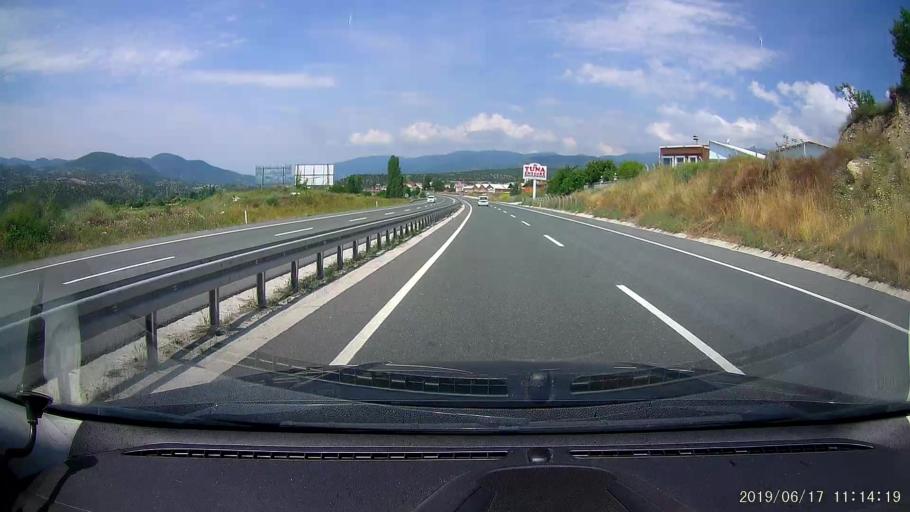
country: TR
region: Kastamonu
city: Tosya
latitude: 40.9576
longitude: 33.9512
